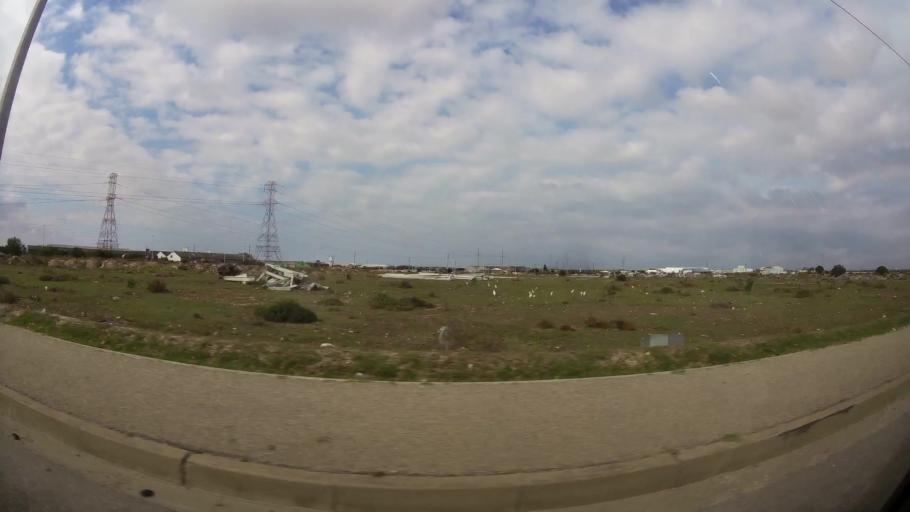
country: ZA
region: Eastern Cape
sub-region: Nelson Mandela Bay Metropolitan Municipality
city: Port Elizabeth
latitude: -33.8048
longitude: 25.6201
